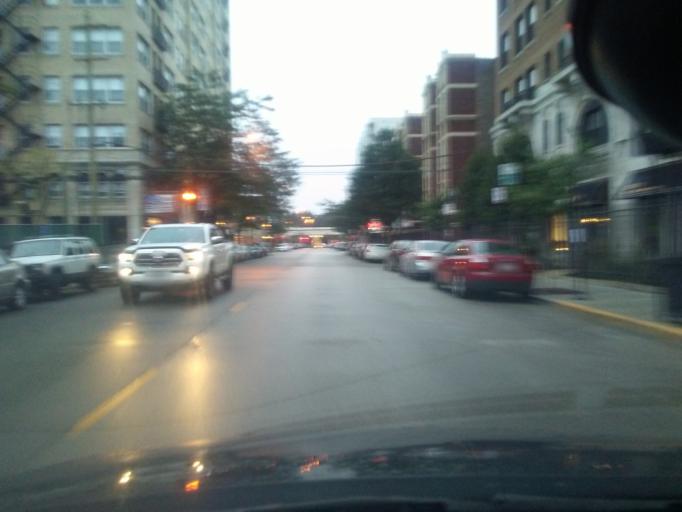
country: US
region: Illinois
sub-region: Cook County
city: Evanston
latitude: 41.9946
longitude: -87.6572
